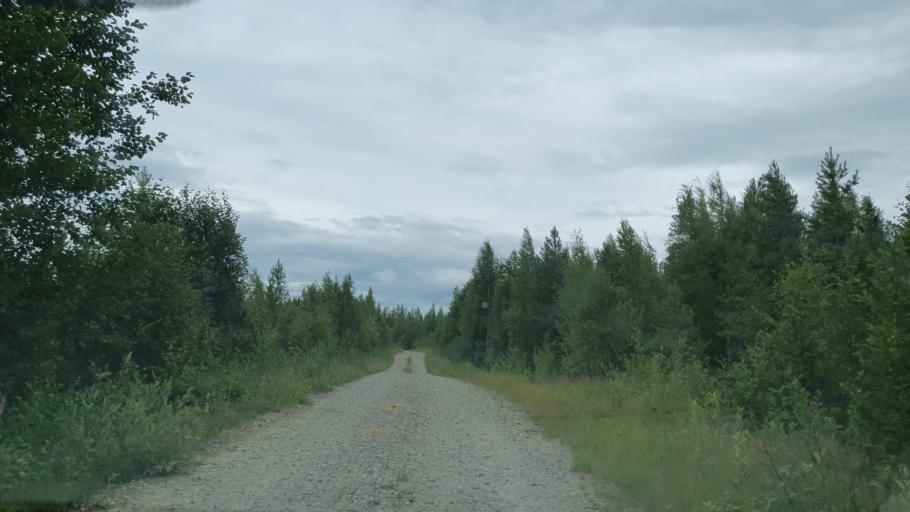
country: FI
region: Kainuu
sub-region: Kehys-Kainuu
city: Kuhmo
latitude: 64.2026
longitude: 29.4023
